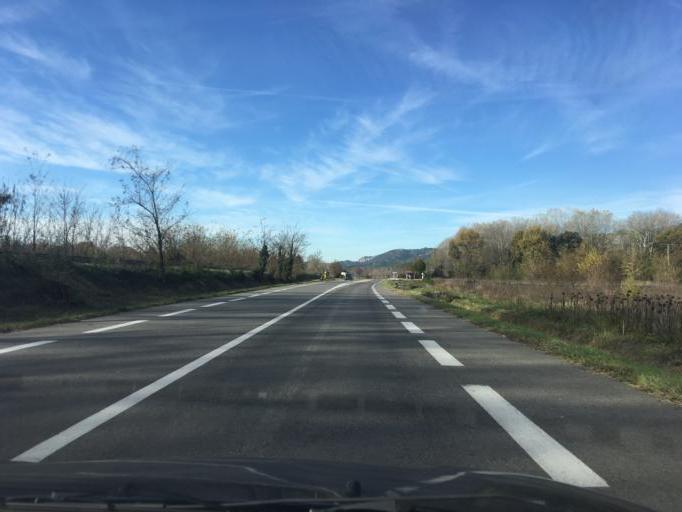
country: FR
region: Provence-Alpes-Cote d'Azur
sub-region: Departement des Bouches-du-Rhone
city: Charleval
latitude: 43.7517
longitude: 5.2614
